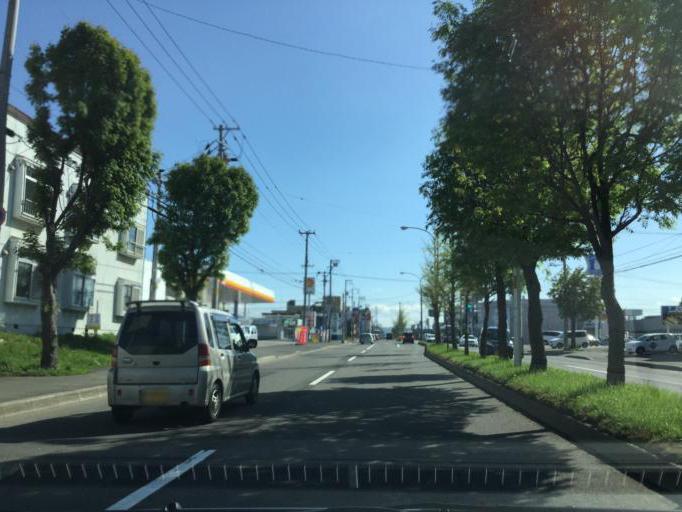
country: JP
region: Hokkaido
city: Sapporo
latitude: 43.0190
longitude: 141.4545
